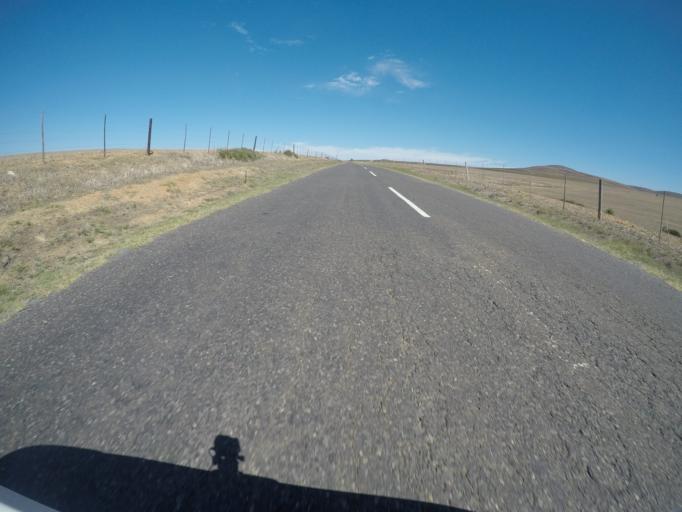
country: ZA
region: Western Cape
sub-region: City of Cape Town
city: Atlantis
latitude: -33.7014
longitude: 18.5878
